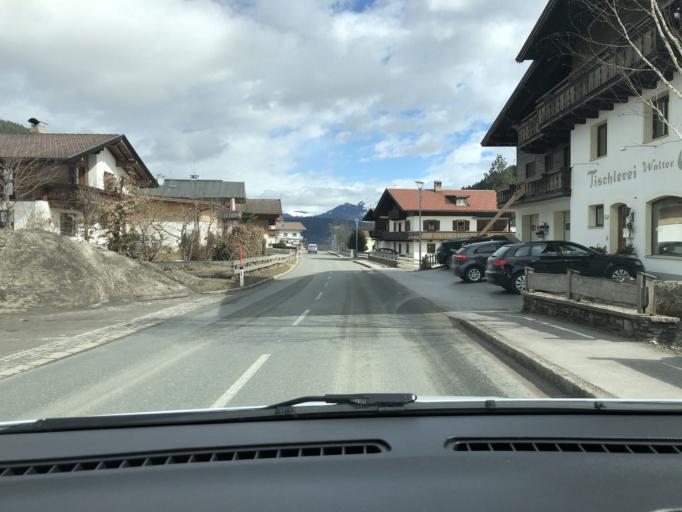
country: AT
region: Tyrol
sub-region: Politischer Bezirk Kufstein
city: Wildschoenau
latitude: 47.4449
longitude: 12.0509
